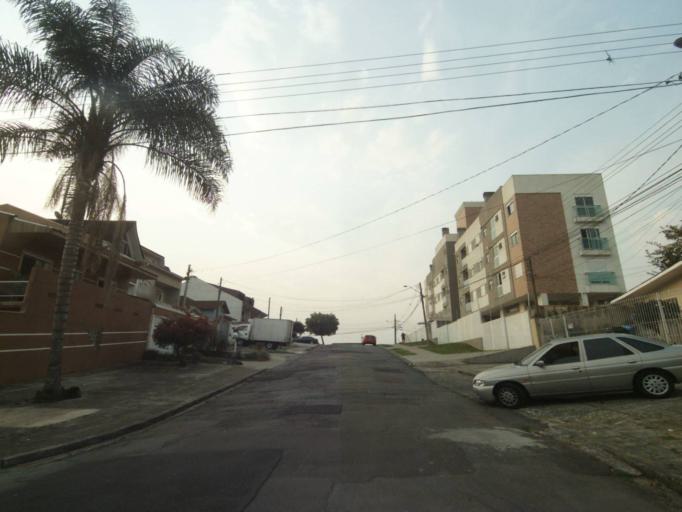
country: BR
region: Parana
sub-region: Curitiba
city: Curitiba
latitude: -25.4760
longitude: -49.2827
